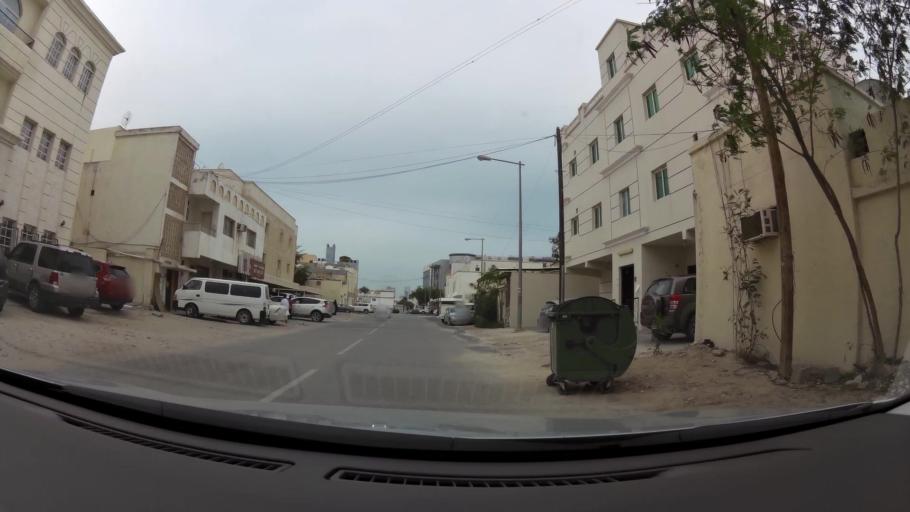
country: QA
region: Baladiyat ad Dawhah
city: Doha
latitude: 25.3134
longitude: 51.4928
